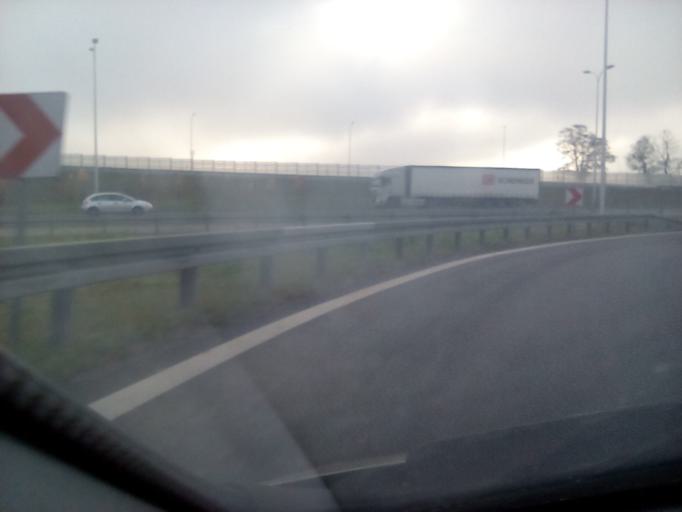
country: PL
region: Masovian Voivodeship
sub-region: Powiat pruszkowski
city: Nowe Grocholice
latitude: 52.1751
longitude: 20.9121
